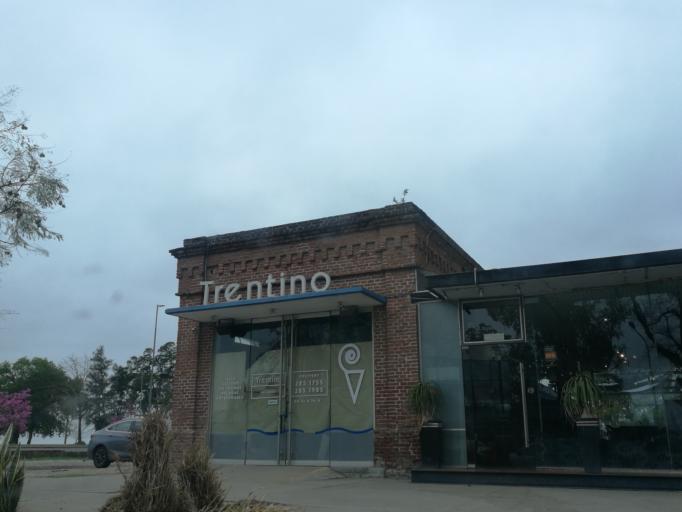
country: AR
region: Santa Fe
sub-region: Departamento de Rosario
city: Rosario
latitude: -32.9311
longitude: -60.6500
